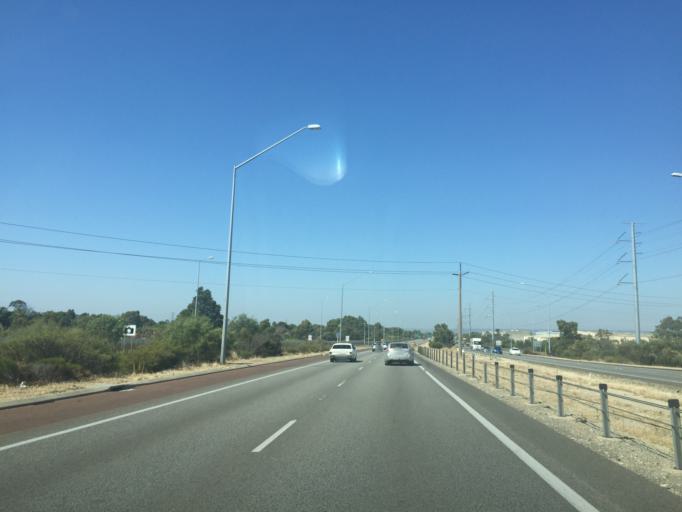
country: AU
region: Western Australia
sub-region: Canning
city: Willetton
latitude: -32.0674
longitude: 115.8918
